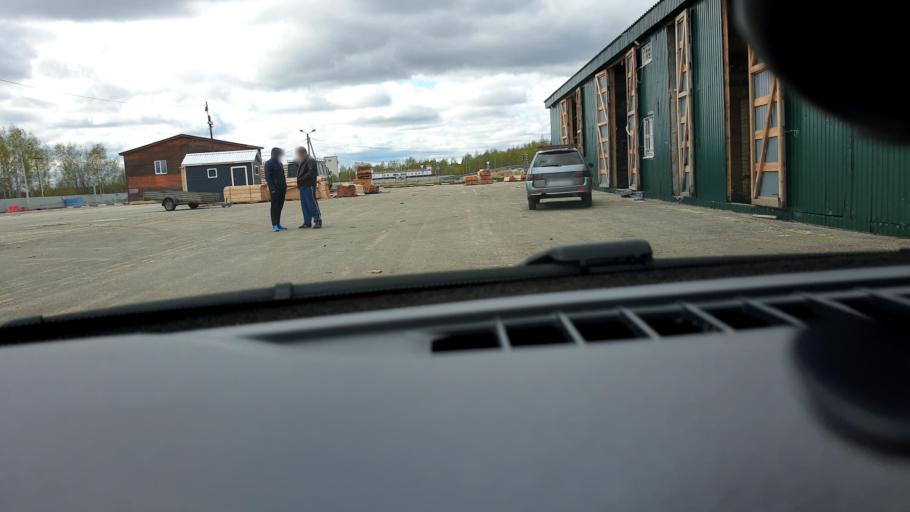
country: RU
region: Nizjnij Novgorod
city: Gorbatovka
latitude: 56.3092
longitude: 43.7930
